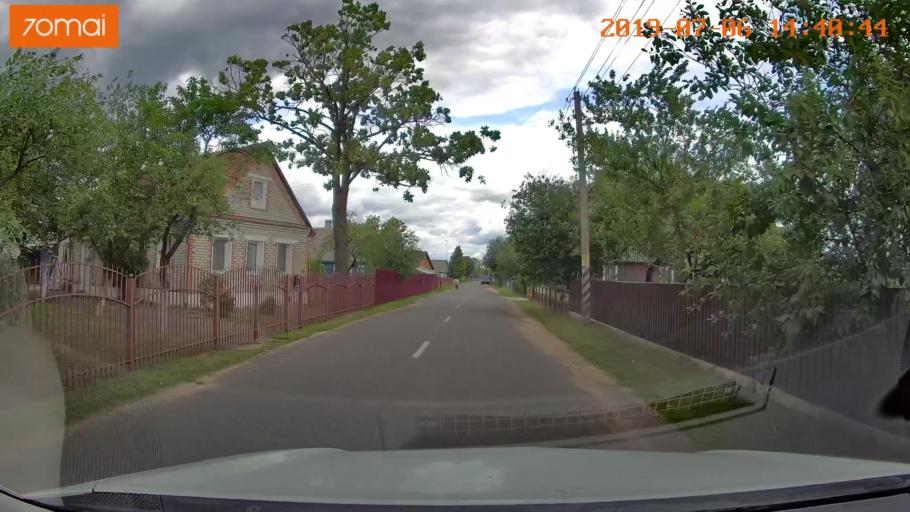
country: BY
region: Minsk
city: Ivyanyets
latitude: 53.9260
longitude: 26.6735
